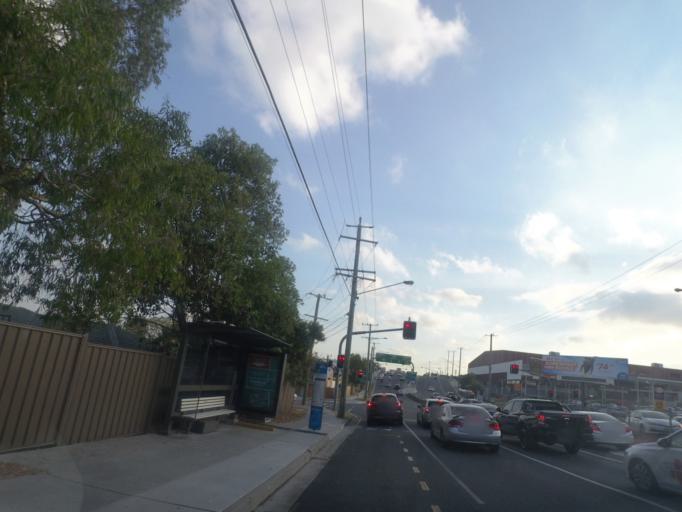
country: AU
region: Queensland
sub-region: Brisbane
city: Nathan
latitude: -27.5582
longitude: 153.0668
